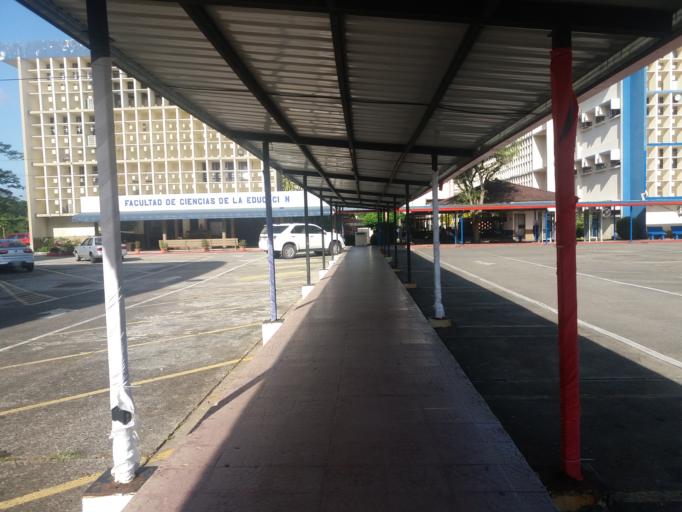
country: PA
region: Panama
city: Panama
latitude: 8.9822
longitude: -79.5369
